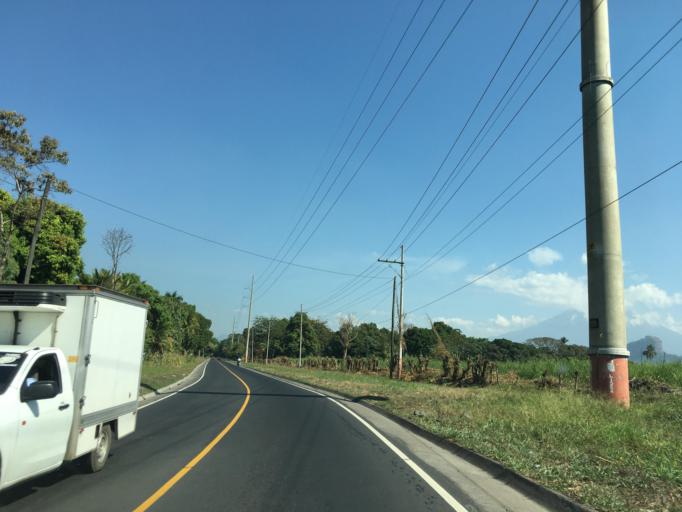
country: GT
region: Escuintla
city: Siquinala
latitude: 14.2885
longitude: -90.9689
